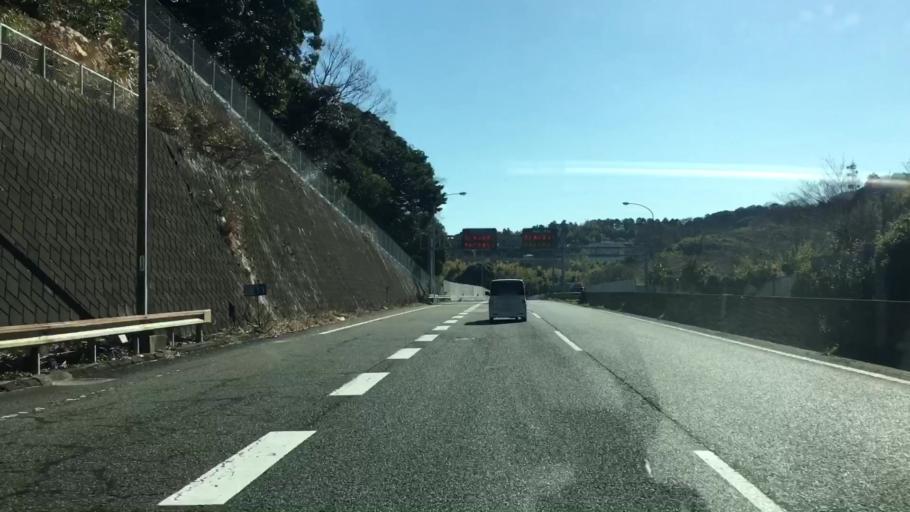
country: JP
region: Kanagawa
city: Kamakura
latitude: 35.3668
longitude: 139.5967
